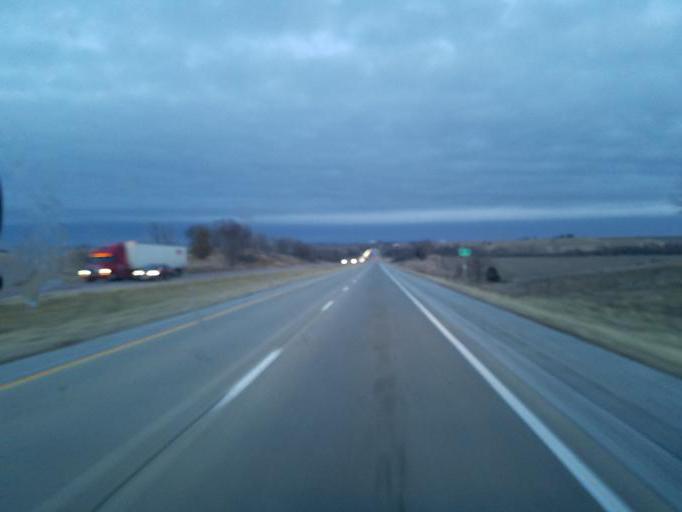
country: US
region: Iowa
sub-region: Cass County
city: Atlantic
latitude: 41.4980
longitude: -95.1553
